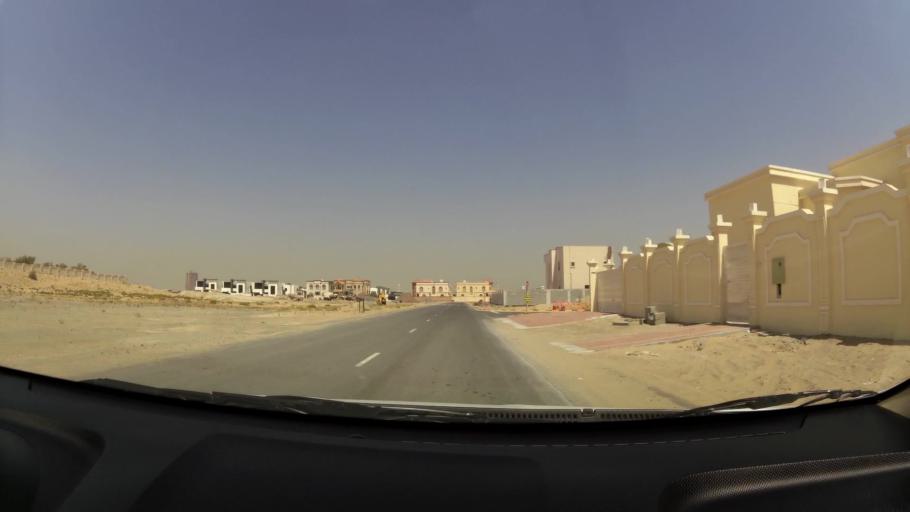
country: AE
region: Ajman
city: Ajman
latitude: 25.4058
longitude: 55.5308
